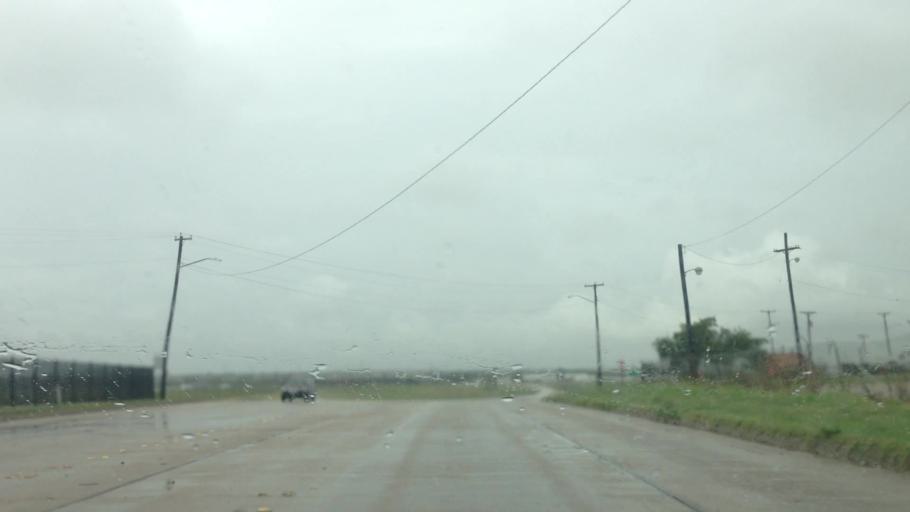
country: US
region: Texas
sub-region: Tarrant County
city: Saginaw
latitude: 32.8312
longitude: -97.3594
